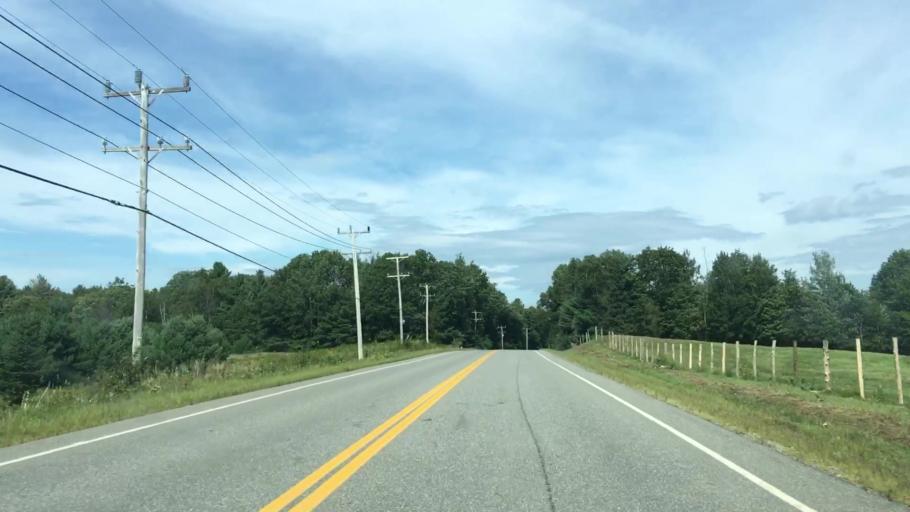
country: US
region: Maine
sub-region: Penobscot County
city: Lincoln
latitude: 45.3993
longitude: -68.5095
